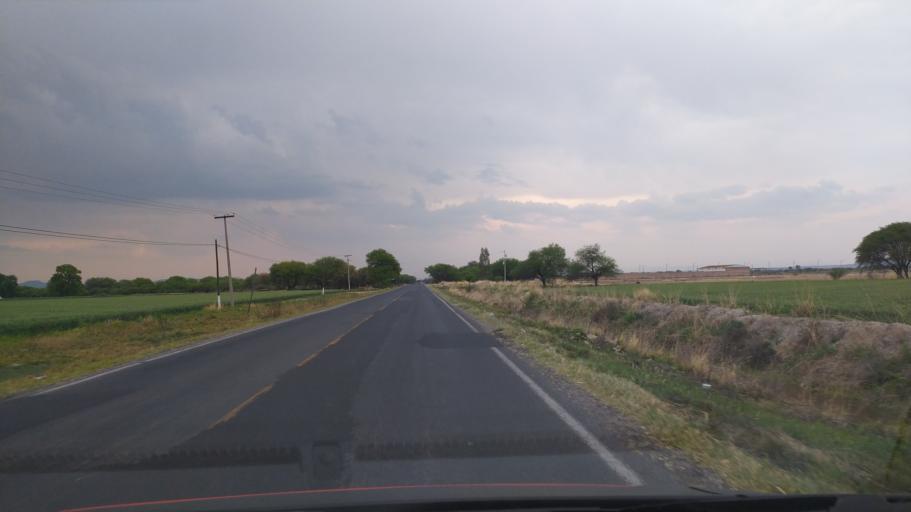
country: MX
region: Guanajuato
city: Ciudad Manuel Doblado
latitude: 20.7630
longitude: -101.9155
